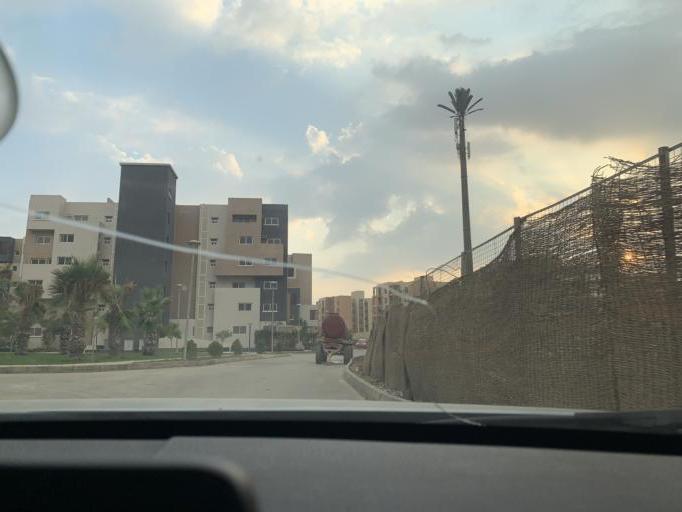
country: EG
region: Muhafazat al Qalyubiyah
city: Al Khankah
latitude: 30.0999
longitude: 31.6521
